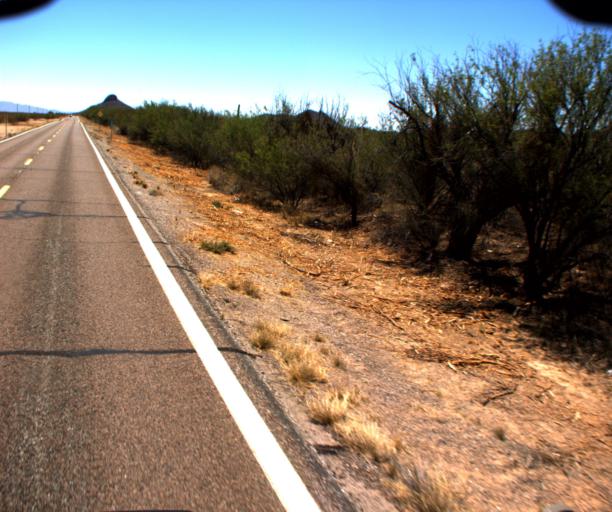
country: US
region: Arizona
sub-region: Pima County
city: Ajo
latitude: 32.2058
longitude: -112.5661
